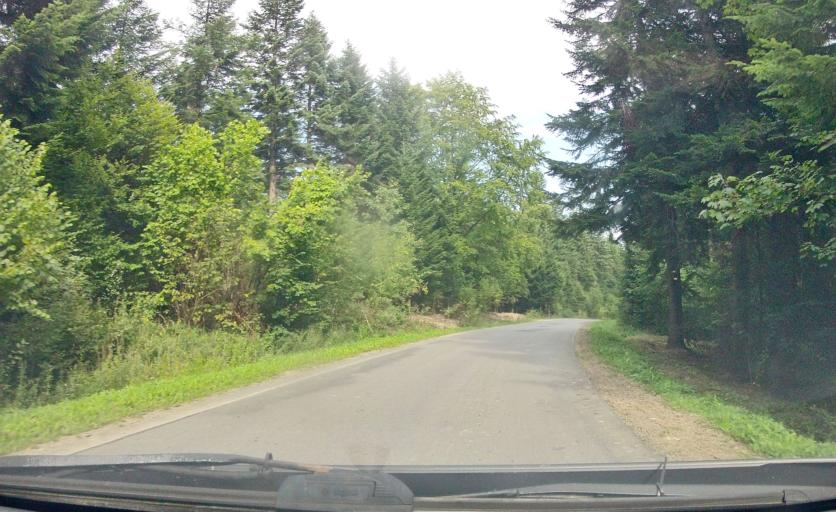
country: PL
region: Subcarpathian Voivodeship
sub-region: Powiat krosnienski
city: Dukla
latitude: 49.5014
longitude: 21.6144
